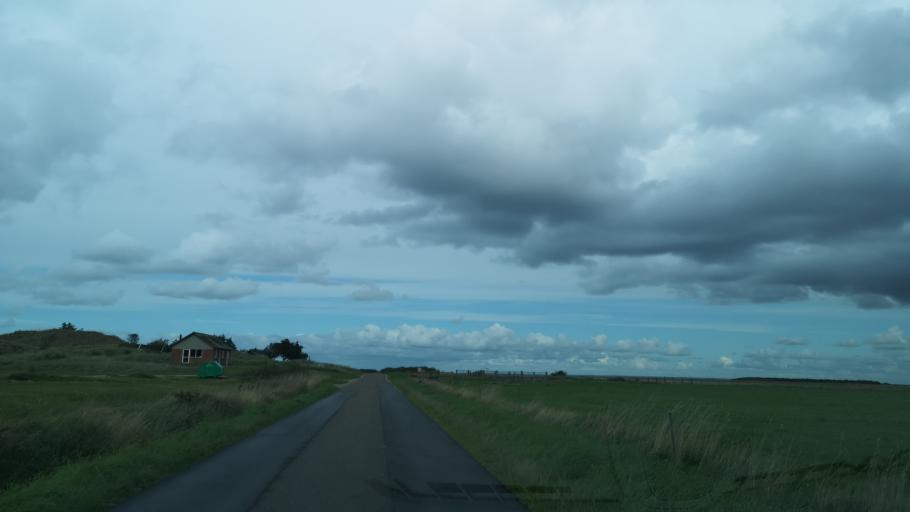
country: DK
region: Central Jutland
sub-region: Ringkobing-Skjern Kommune
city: Hvide Sande
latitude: 55.8505
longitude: 8.2182
